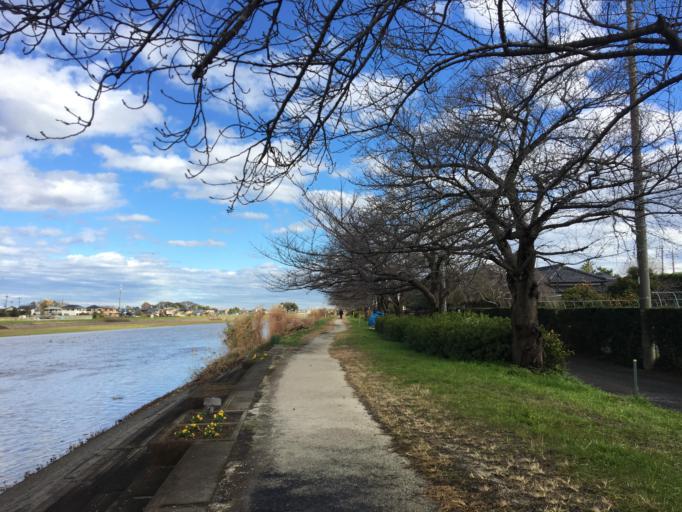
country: JP
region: Saitama
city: Koshigaya
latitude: 35.9252
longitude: 139.8075
